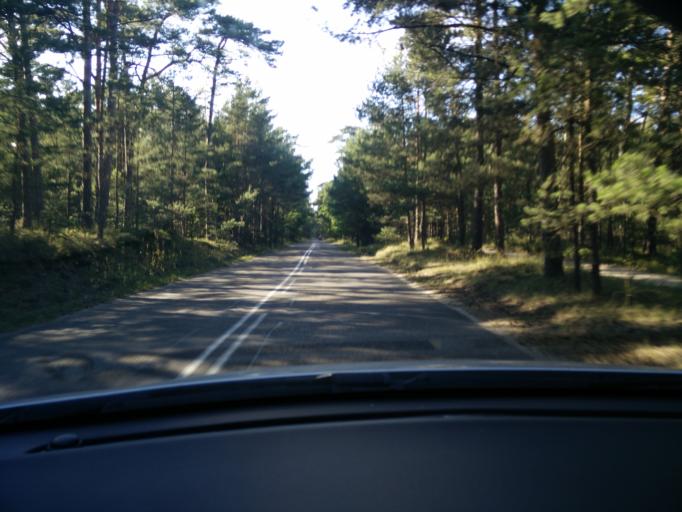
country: PL
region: Pomeranian Voivodeship
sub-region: Powiat pucki
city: Jastarnia
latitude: 54.6650
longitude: 18.7453
